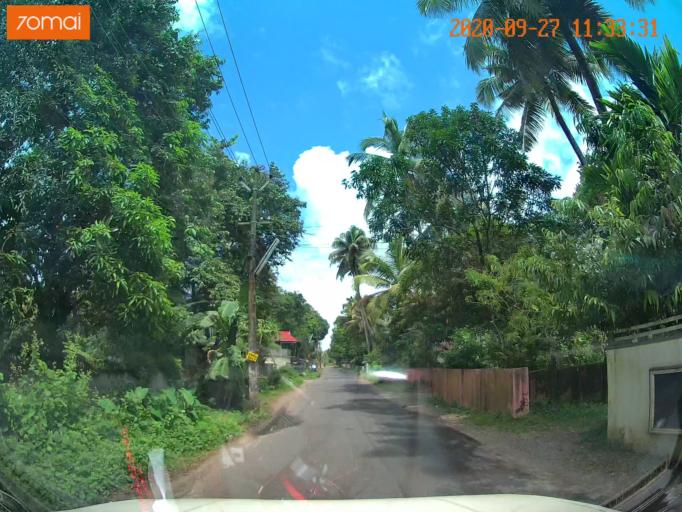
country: IN
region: Kerala
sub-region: Thrissur District
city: Thanniyam
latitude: 10.4314
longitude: 76.1290
